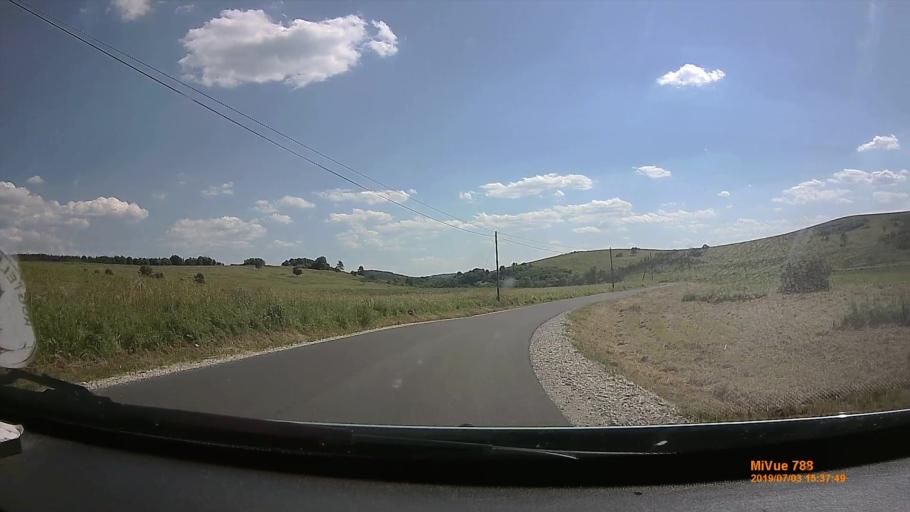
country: HU
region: Heves
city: Szilvasvarad
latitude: 48.1754
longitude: 20.4008
